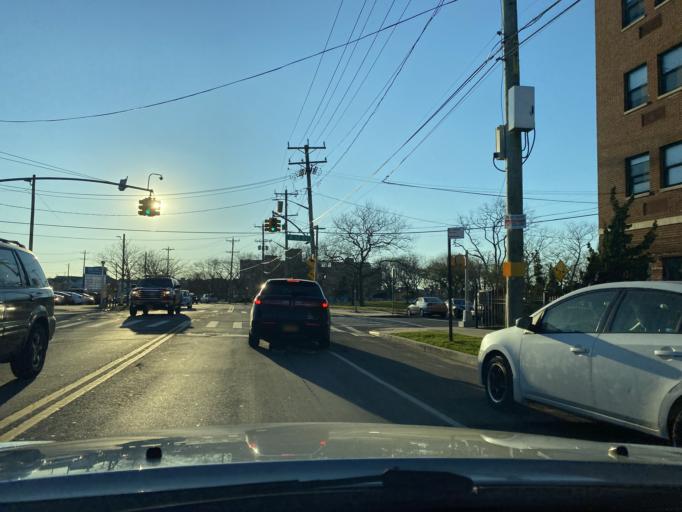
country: US
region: New York
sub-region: Nassau County
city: Inwood
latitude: 40.5989
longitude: -73.7657
